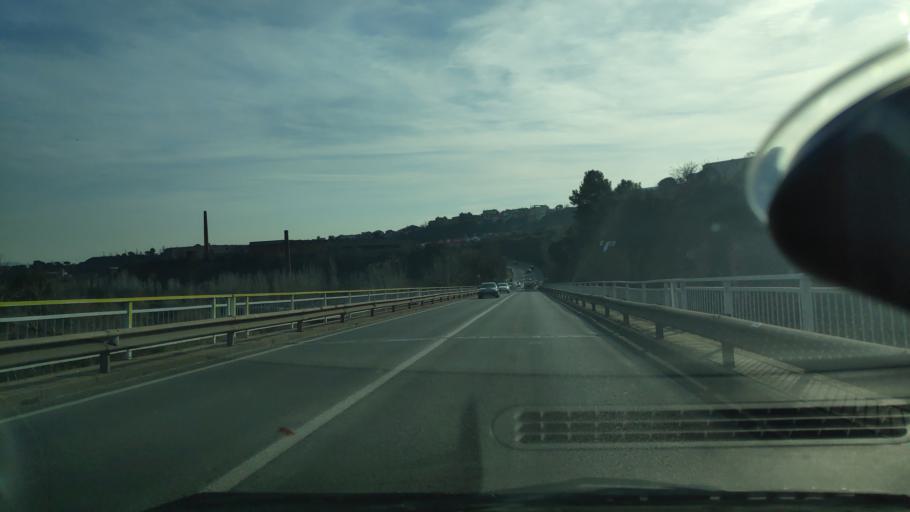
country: ES
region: Catalonia
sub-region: Provincia de Barcelona
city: Sabadell
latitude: 41.5761
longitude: 2.0938
